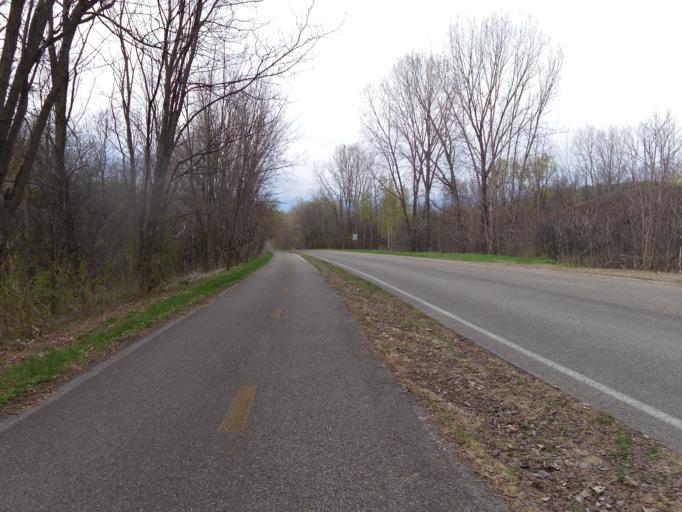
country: CA
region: Quebec
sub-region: Laurentides
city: Oka
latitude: 45.4900
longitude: -74.0158
